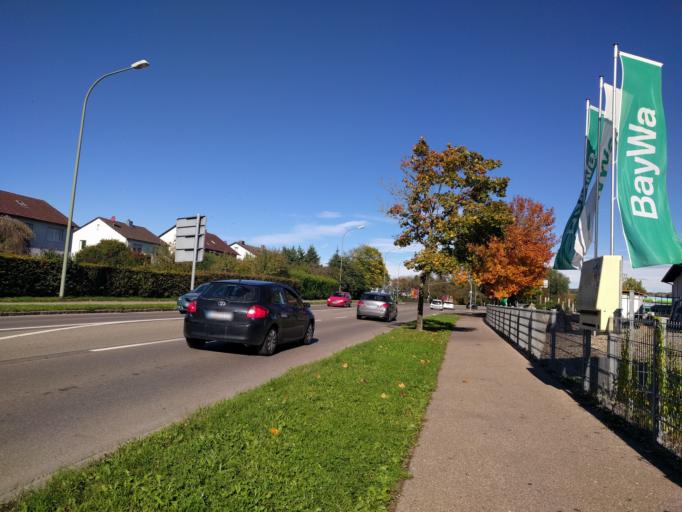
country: DE
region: Bavaria
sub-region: Swabia
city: Donauwoerth
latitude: 48.7187
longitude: 10.7614
